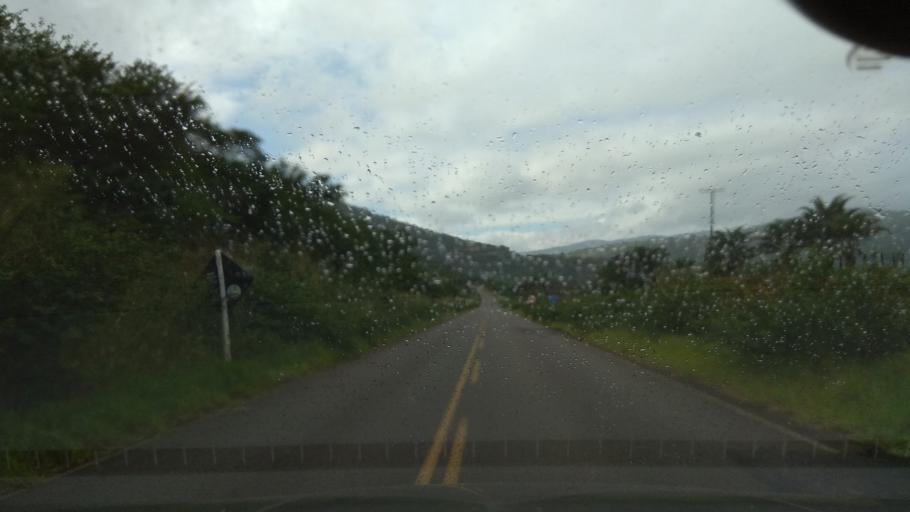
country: BR
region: Bahia
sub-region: Ubaira
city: Ubaira
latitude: -13.2487
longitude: -39.7374
